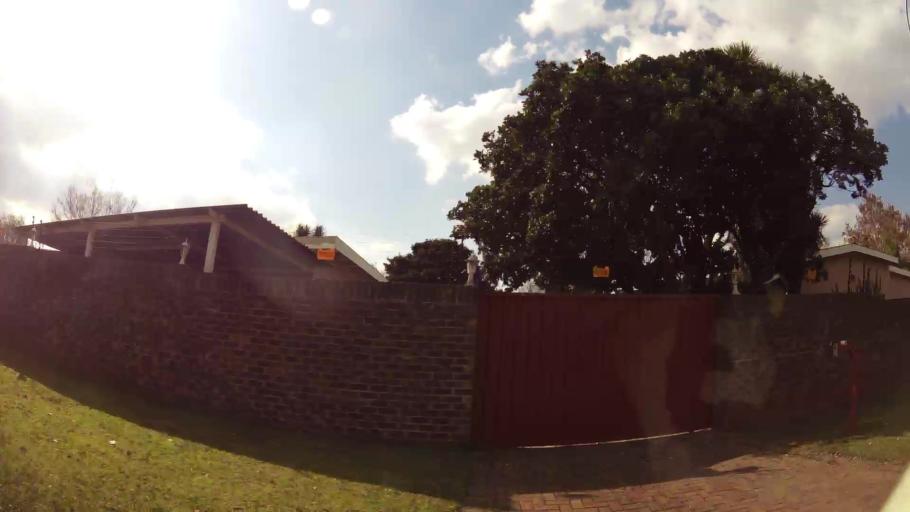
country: ZA
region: Mpumalanga
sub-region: Nkangala District Municipality
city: Delmas
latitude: -26.1417
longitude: 28.6772
